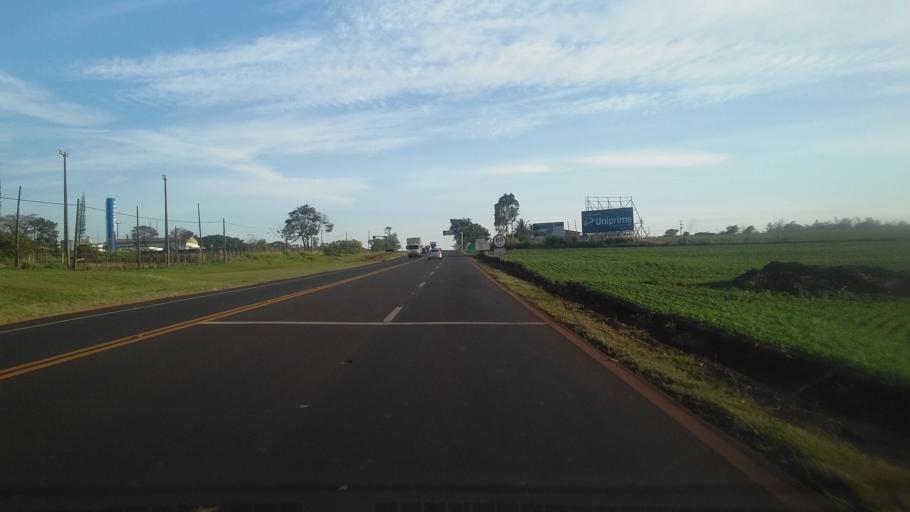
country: BR
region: Parana
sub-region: Assai
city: Assai
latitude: -23.2218
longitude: -50.6714
